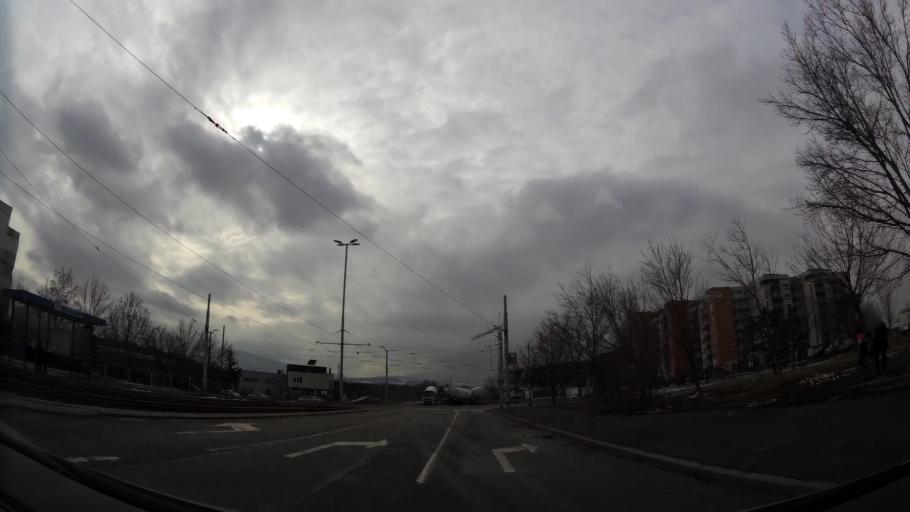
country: BG
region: Sofiya
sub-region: Obshtina Bozhurishte
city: Bozhurishte
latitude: 42.7104
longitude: 23.2456
